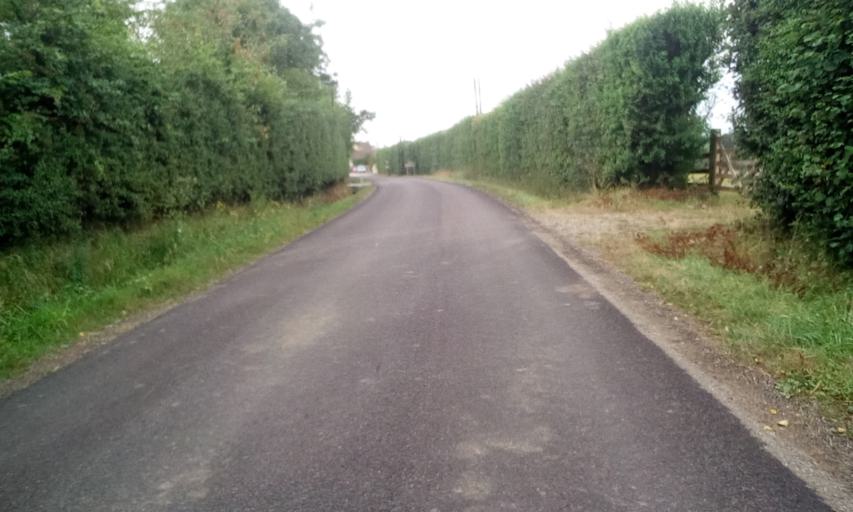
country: FR
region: Lower Normandy
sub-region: Departement du Calvados
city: Troarn
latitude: 49.1879
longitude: -0.1581
